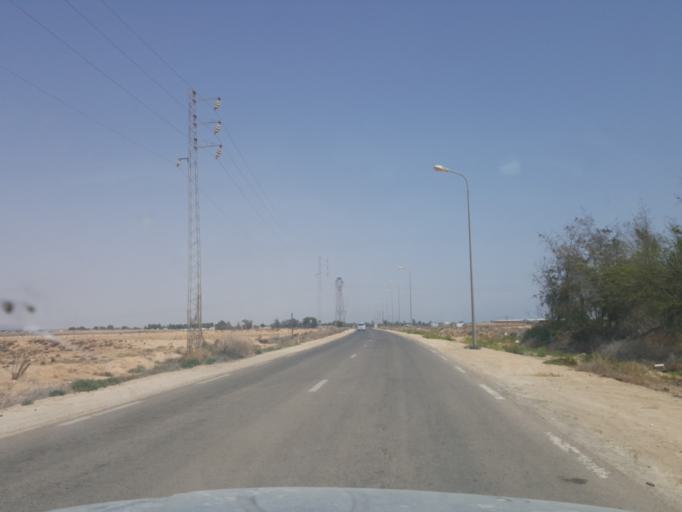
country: TN
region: Qabis
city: Gabes
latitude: 33.9735
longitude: 10.0018
